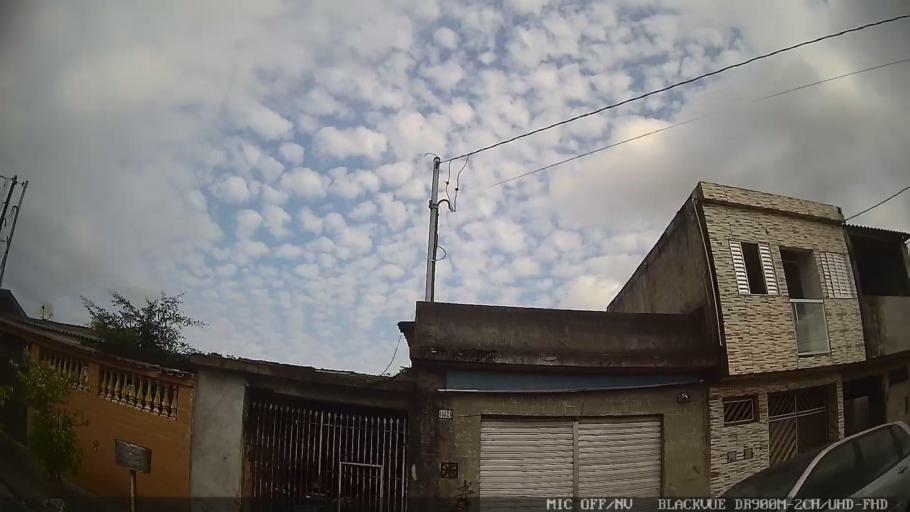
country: BR
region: Sao Paulo
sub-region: Guaruja
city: Guaruja
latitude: -23.9571
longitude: -46.2765
